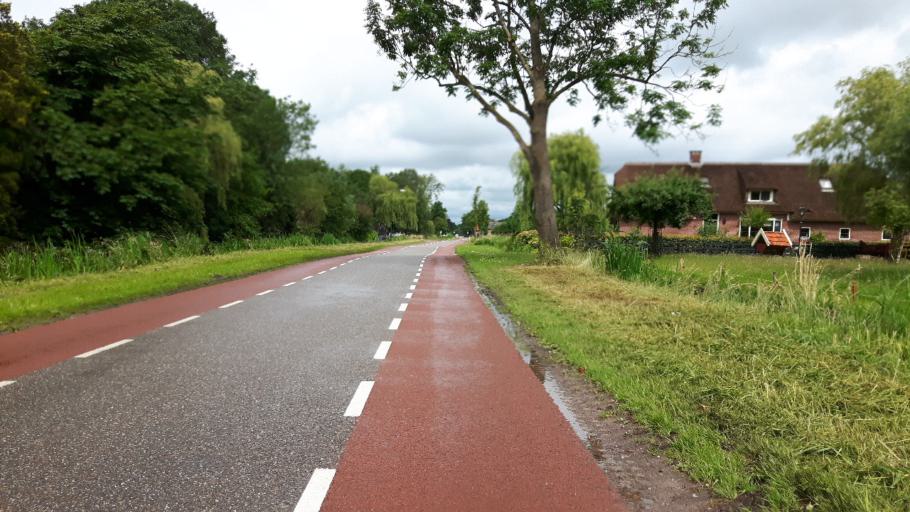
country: NL
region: Utrecht
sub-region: Stichtse Vecht
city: Breukelen
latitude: 52.1689
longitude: 4.9490
